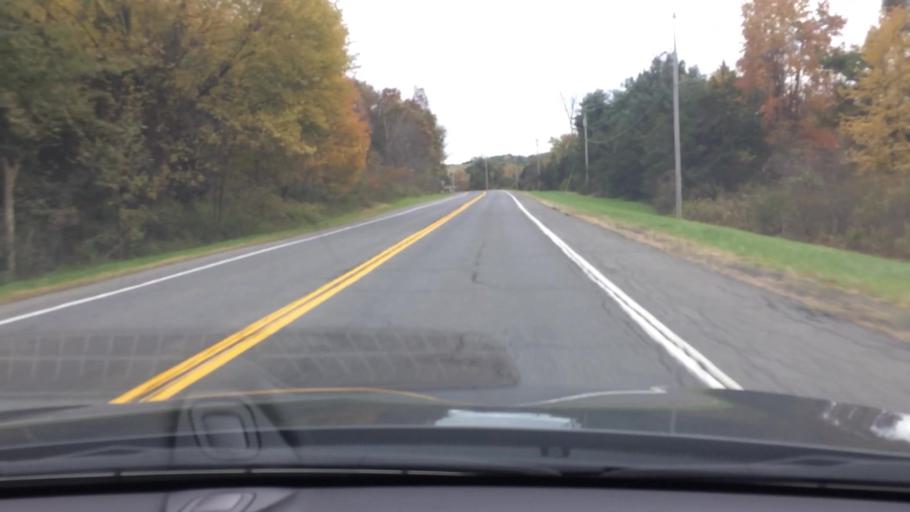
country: US
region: New York
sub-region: Columbia County
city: Oakdale
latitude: 42.1298
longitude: -73.7285
